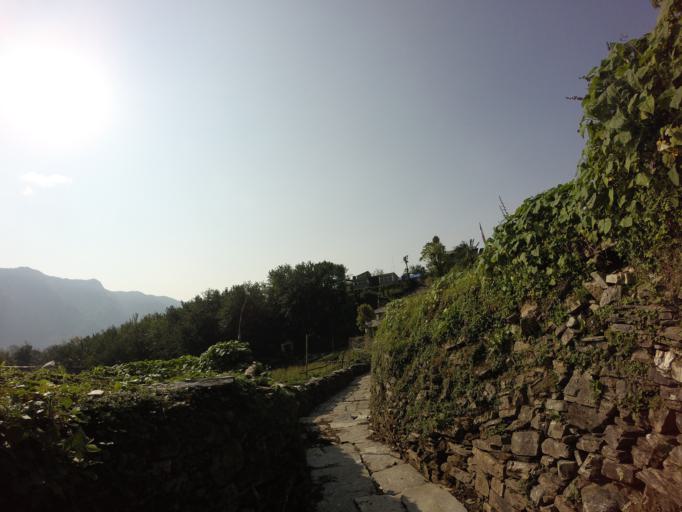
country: NP
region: Western Region
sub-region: Dhawalagiri Zone
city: Chitre
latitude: 28.3764
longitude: 83.8099
